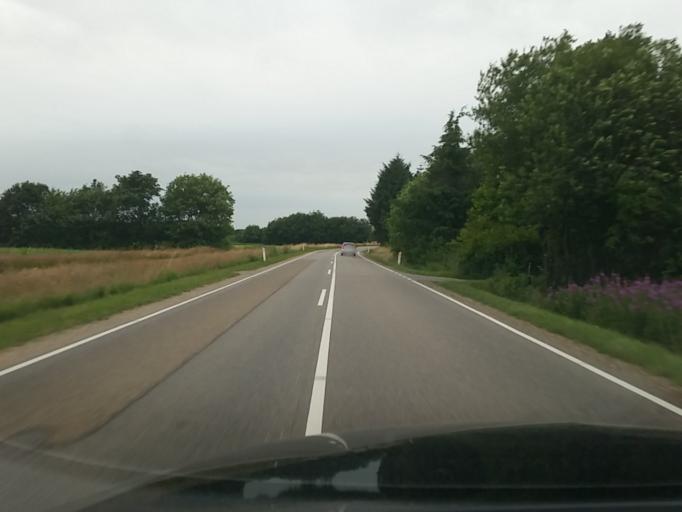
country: DK
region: South Denmark
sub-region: Billund Kommune
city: Grindsted
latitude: 55.6569
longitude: 8.7980
